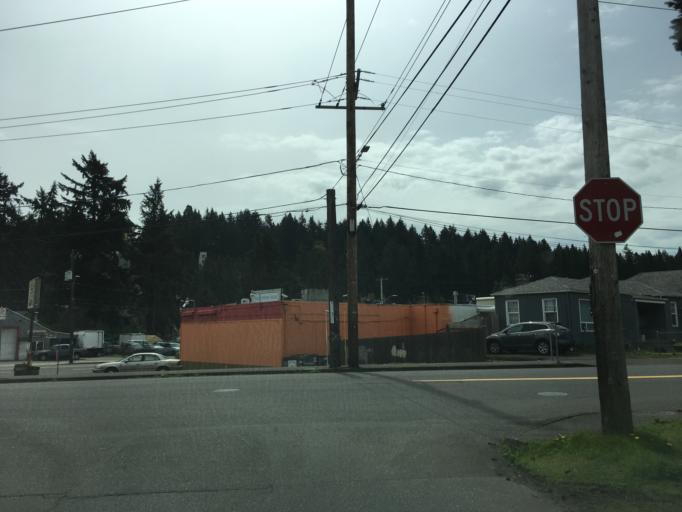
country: US
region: Oregon
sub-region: Multnomah County
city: Lents
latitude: 45.5560
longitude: -122.5713
